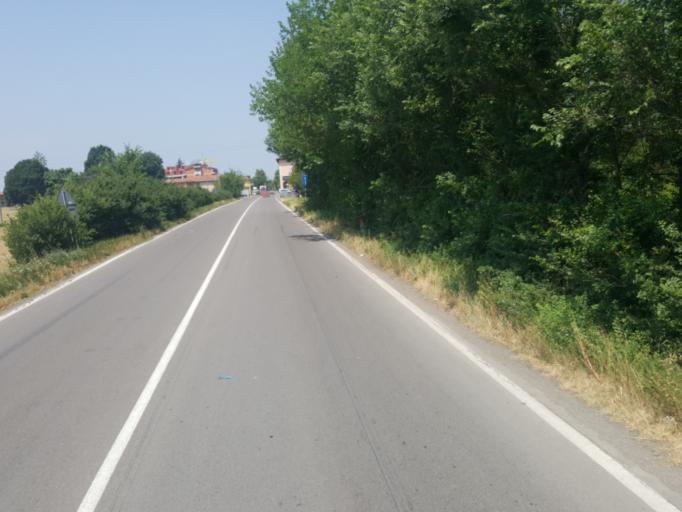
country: IT
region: Emilia-Romagna
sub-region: Provincia di Modena
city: Cavazzona
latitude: 44.5722
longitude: 11.1183
